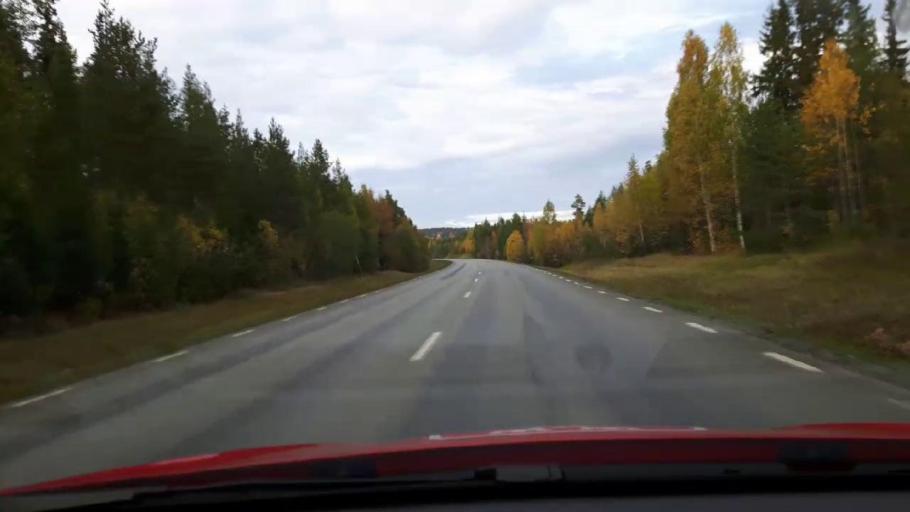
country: SE
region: Jaemtland
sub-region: Krokoms Kommun
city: Krokom
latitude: 63.3433
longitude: 14.4715
